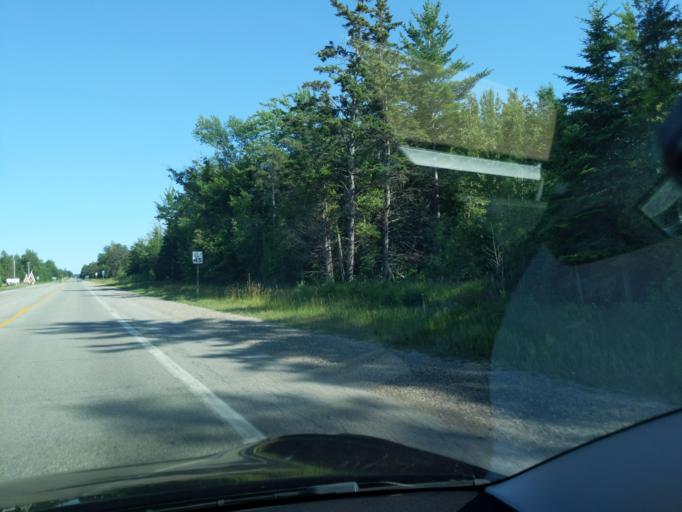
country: US
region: Michigan
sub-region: Mackinac County
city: Saint Ignace
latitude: 45.7644
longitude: -84.7192
